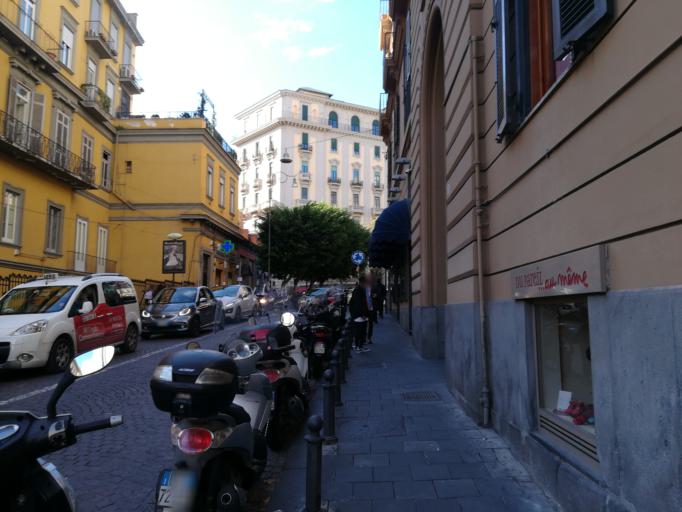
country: IT
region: Campania
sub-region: Provincia di Napoli
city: Napoli
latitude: 40.8368
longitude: 14.2345
